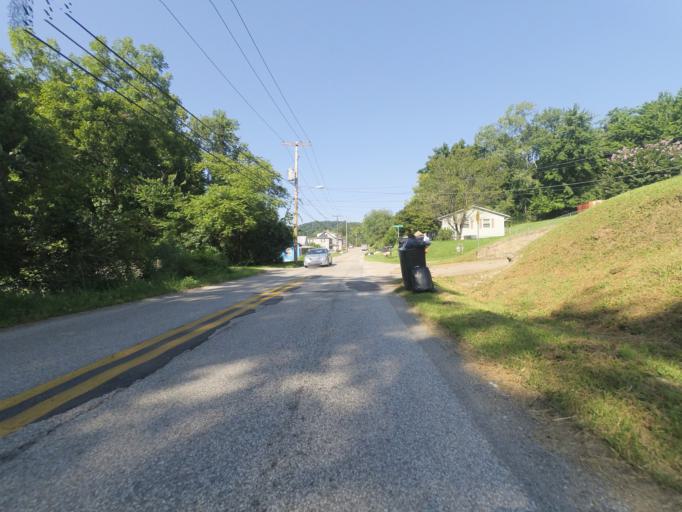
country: US
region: West Virginia
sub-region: Cabell County
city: Huntington
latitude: 38.3998
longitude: -82.4645
